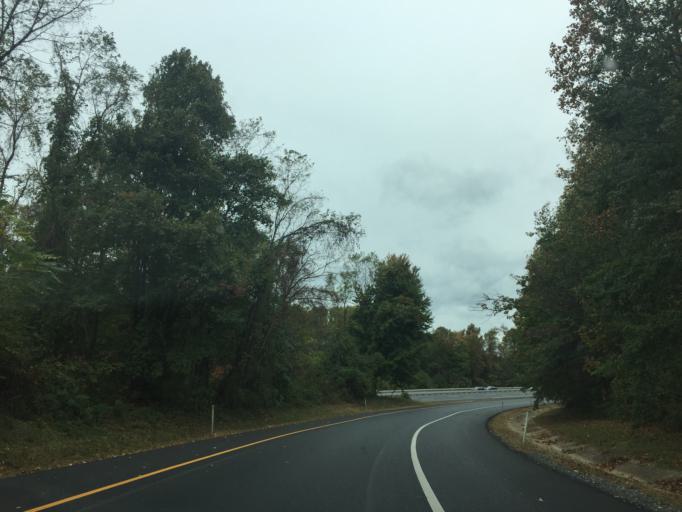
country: US
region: Maryland
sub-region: Harford County
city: Havre de Grace
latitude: 39.5726
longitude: -76.1347
